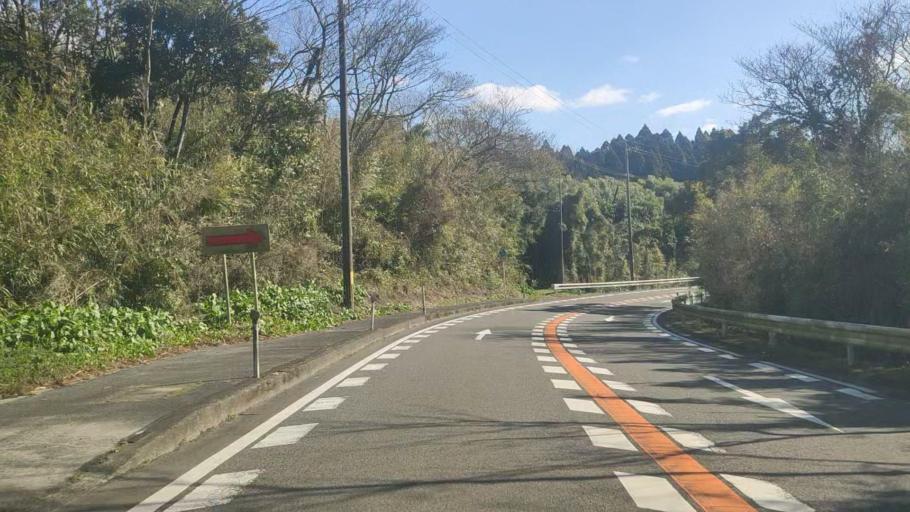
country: JP
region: Kagoshima
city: Kokubu-matsuki
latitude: 31.6661
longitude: 130.8800
